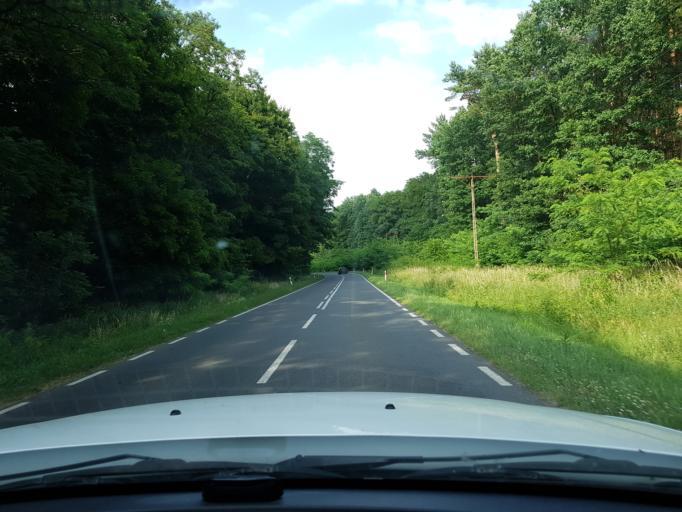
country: PL
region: West Pomeranian Voivodeship
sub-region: Powiat gryfinski
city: Chojna
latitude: 52.9262
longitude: 14.3714
